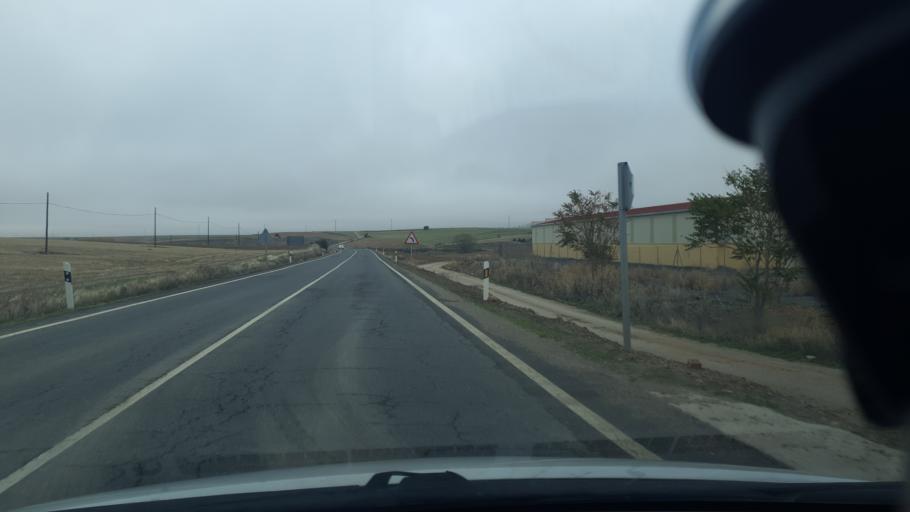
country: ES
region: Castille and Leon
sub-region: Provincia de Segovia
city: Encinillas
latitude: 41.0045
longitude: -4.1512
